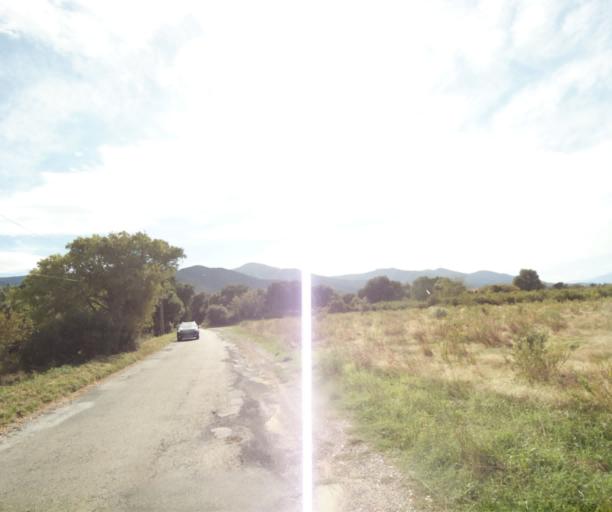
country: FR
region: Languedoc-Roussillon
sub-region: Departement des Pyrenees-Orientales
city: Sant Andreu de Sureda
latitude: 42.5405
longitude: 2.9885
